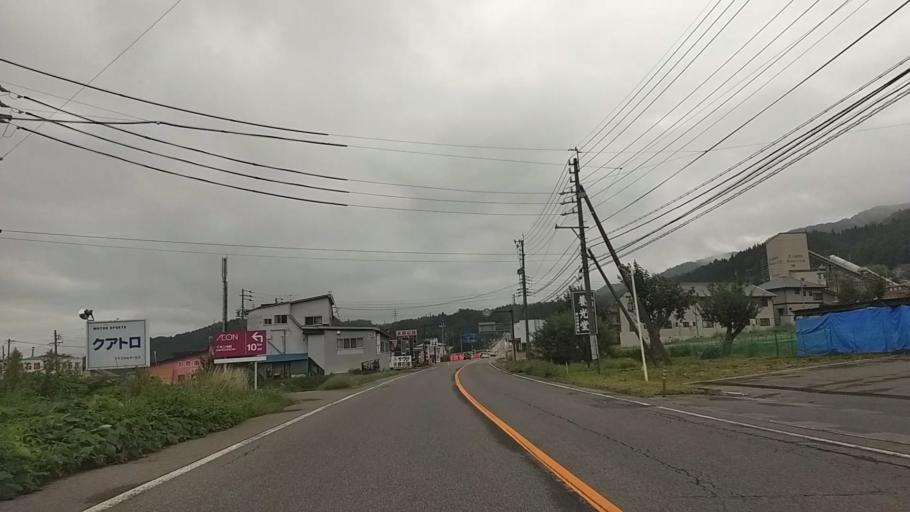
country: JP
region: Nagano
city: Iiyama
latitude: 36.8254
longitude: 138.3529
